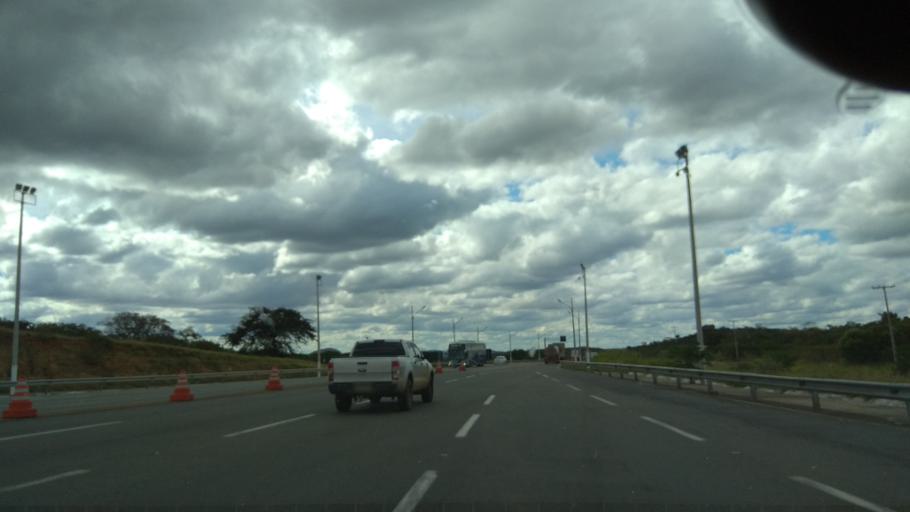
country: BR
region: Bahia
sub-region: Santa Ines
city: Santa Ines
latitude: -13.0080
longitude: -39.9569
